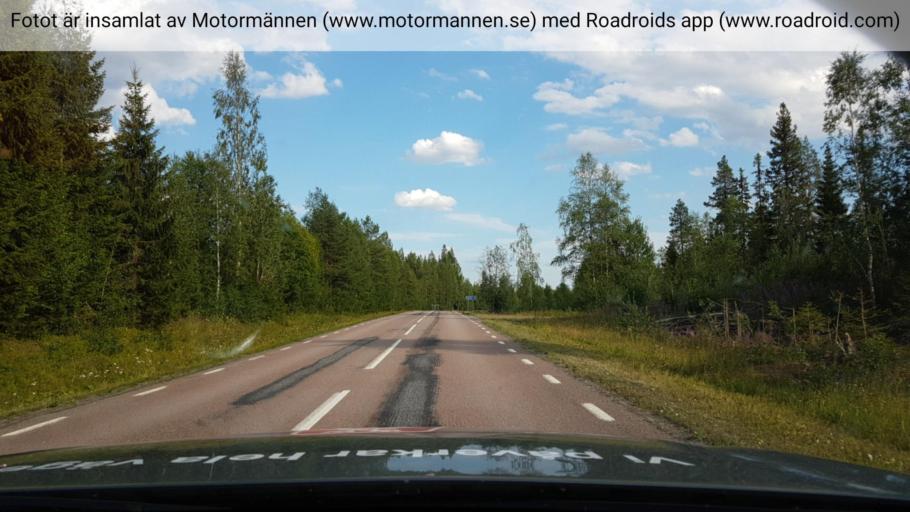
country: SE
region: Jaemtland
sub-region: Stroemsunds Kommun
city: Stroemsund
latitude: 63.6790
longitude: 15.9264
